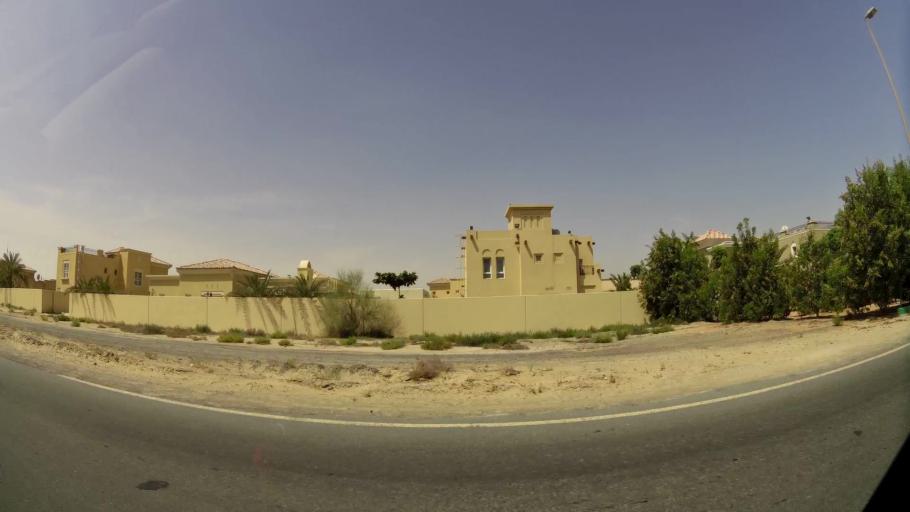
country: AE
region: Ash Shariqah
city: Sharjah
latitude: 25.1821
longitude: 55.4342
